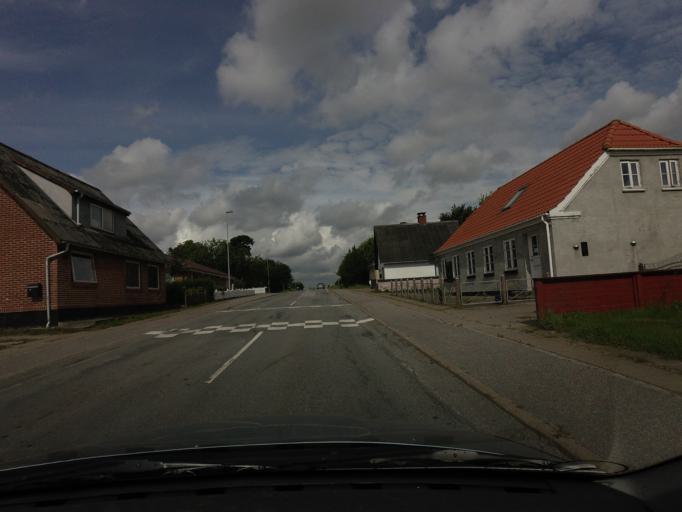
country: DK
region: North Denmark
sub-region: Hjorring Kommune
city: Tars
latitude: 57.3661
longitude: 10.1872
